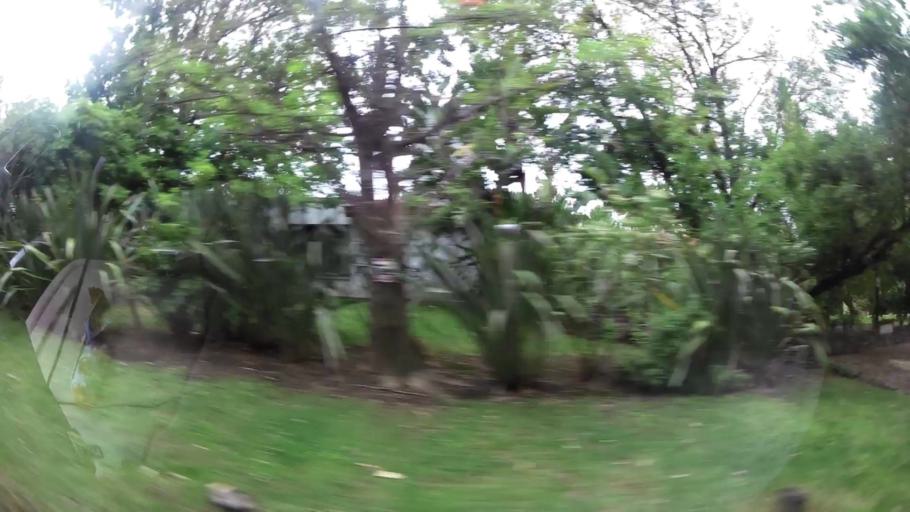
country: UY
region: Maldonado
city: Maldonado
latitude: -34.9037
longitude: -55.0002
